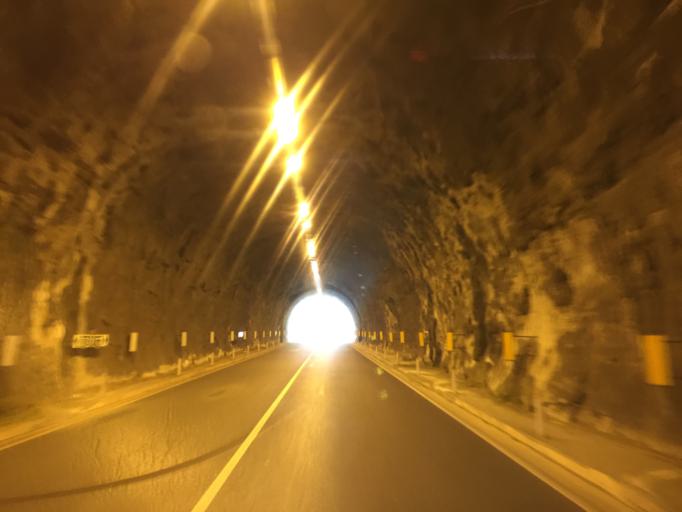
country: ES
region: Asturias
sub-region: Province of Asturias
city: Proaza
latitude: 43.2312
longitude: -6.0345
